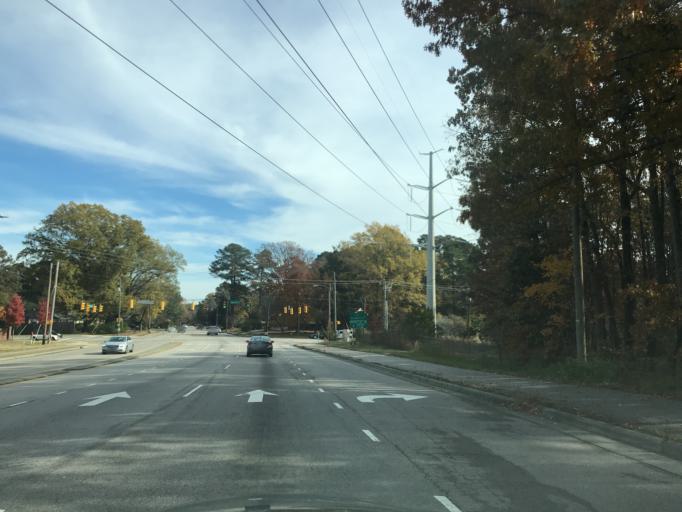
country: US
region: North Carolina
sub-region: Wake County
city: West Raleigh
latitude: 35.8012
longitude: -78.6851
